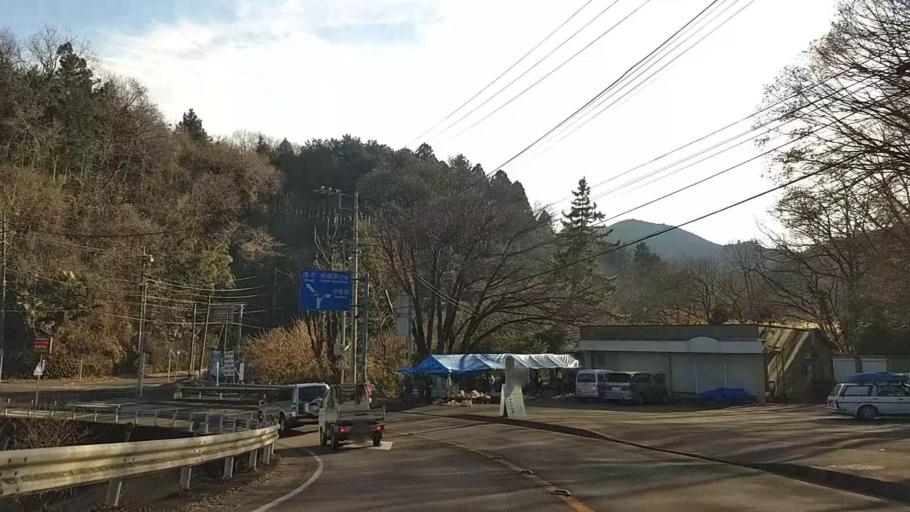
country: JP
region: Yamanashi
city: Uenohara
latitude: 35.5631
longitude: 139.2069
